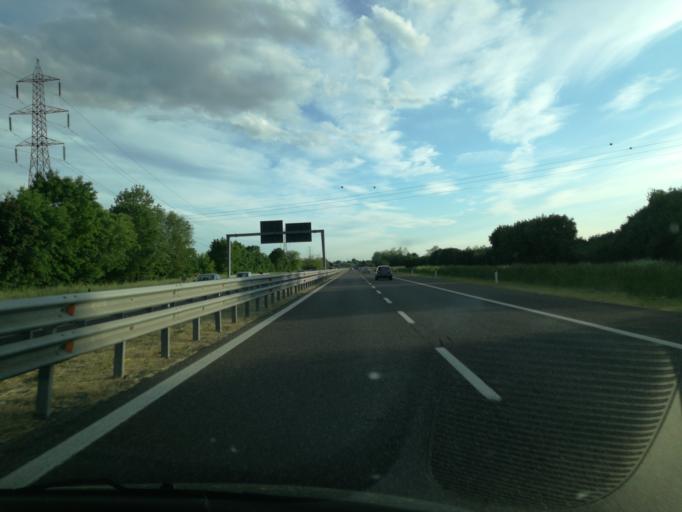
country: IT
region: Lombardy
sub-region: Provincia di Monza e Brianza
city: Agrate Brianza
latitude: 45.5891
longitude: 9.3536
